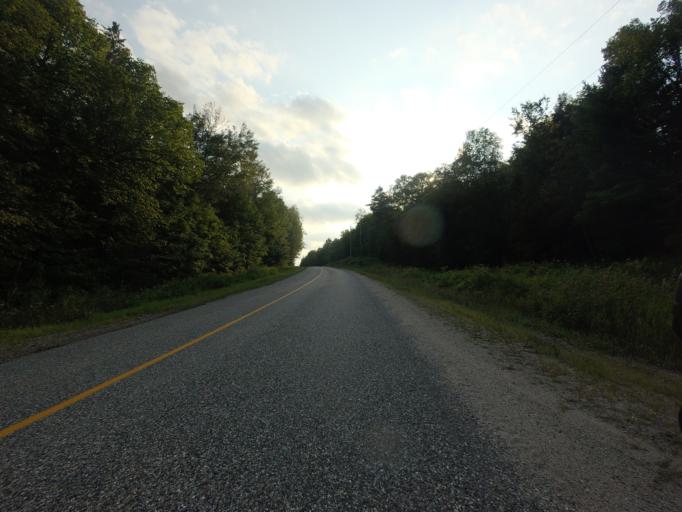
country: CA
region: Ontario
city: Perth
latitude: 44.9670
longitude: -76.7030
